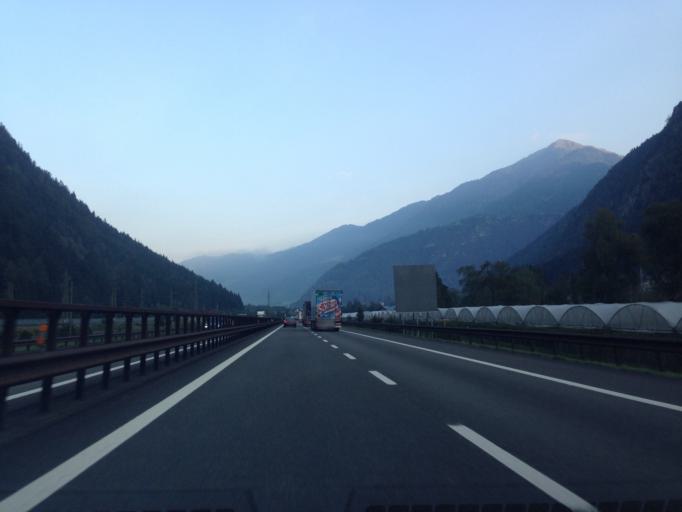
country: IT
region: Trentino-Alto Adige
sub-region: Bolzano
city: Campo di Trens
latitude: 46.8361
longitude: 11.5300
